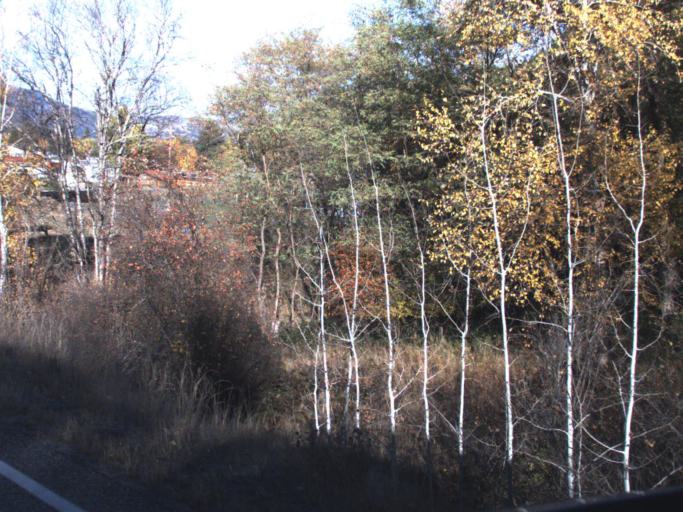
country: CA
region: British Columbia
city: Rossland
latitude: 48.9094
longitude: -117.7917
